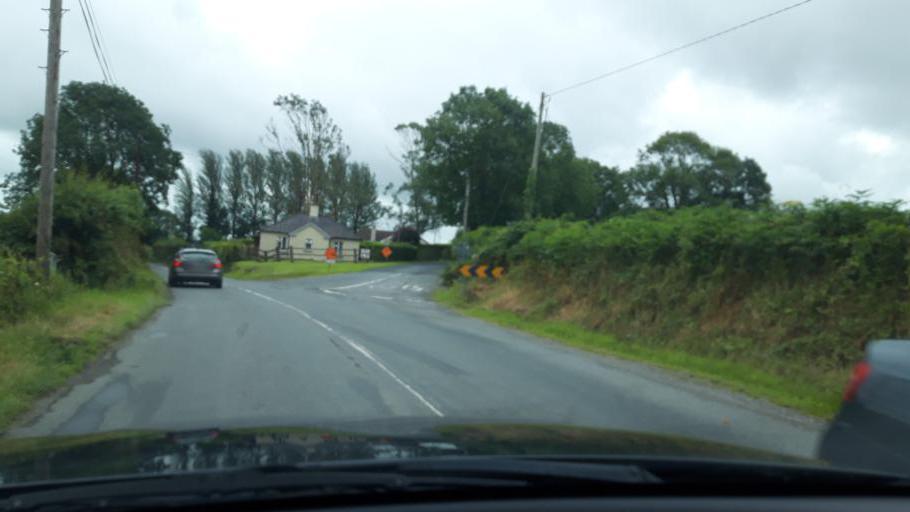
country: IE
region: Munster
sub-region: County Cork
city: Youghal
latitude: 52.1660
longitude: -7.8531
